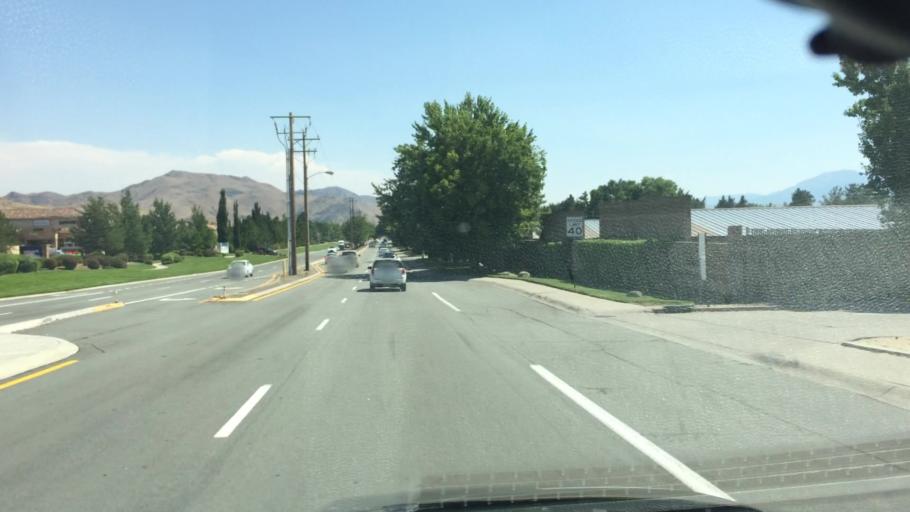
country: US
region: Nevada
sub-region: Washoe County
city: Sparks
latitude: 39.5568
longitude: -119.7057
